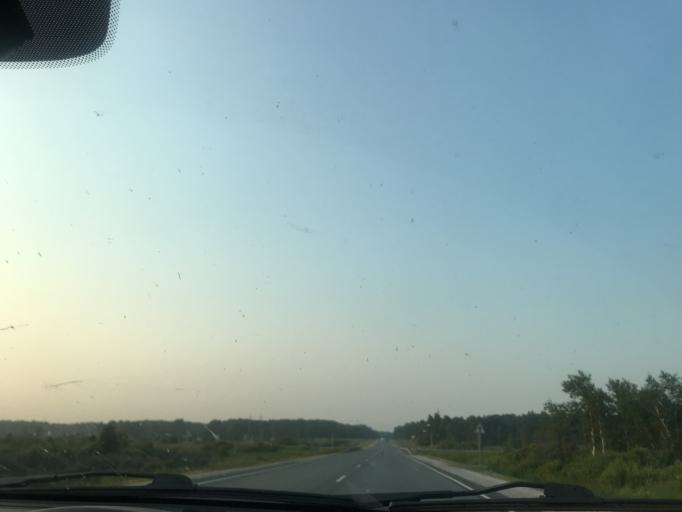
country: RU
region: Novosibirsk
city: Dorogino
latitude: 54.3731
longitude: 83.3042
